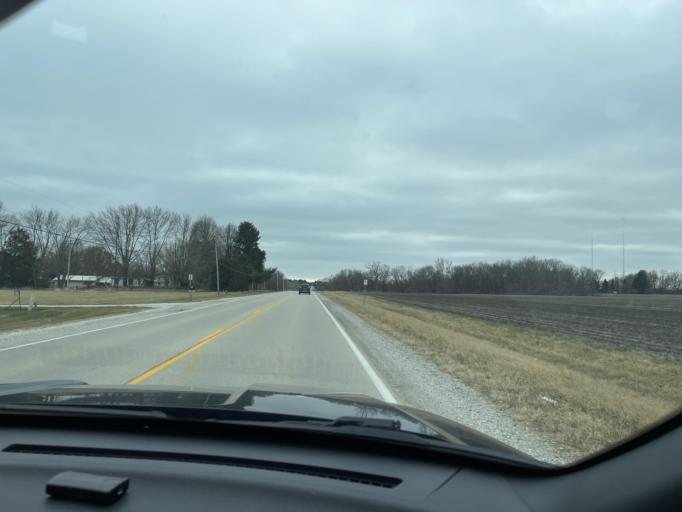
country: US
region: Illinois
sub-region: Sangamon County
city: Leland Grove
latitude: 39.8180
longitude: -89.7397
